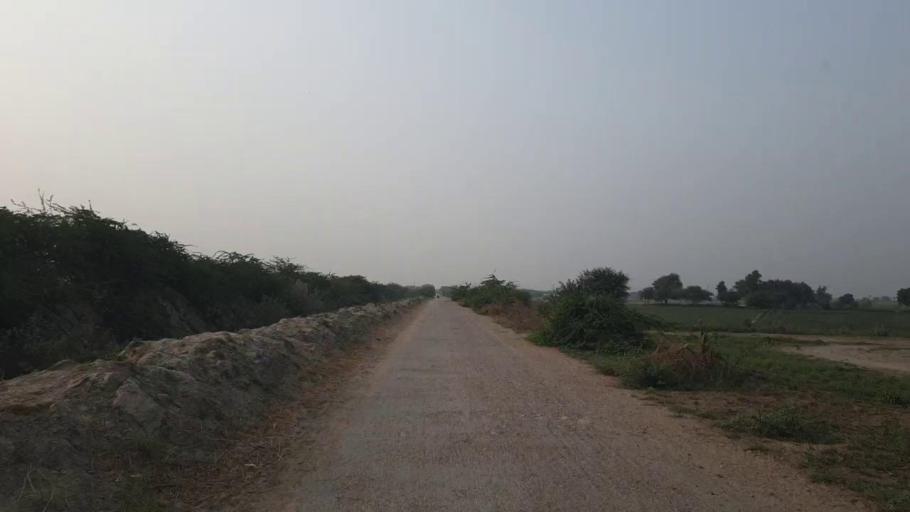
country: PK
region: Sindh
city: Mirpur Batoro
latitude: 24.6466
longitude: 68.3924
